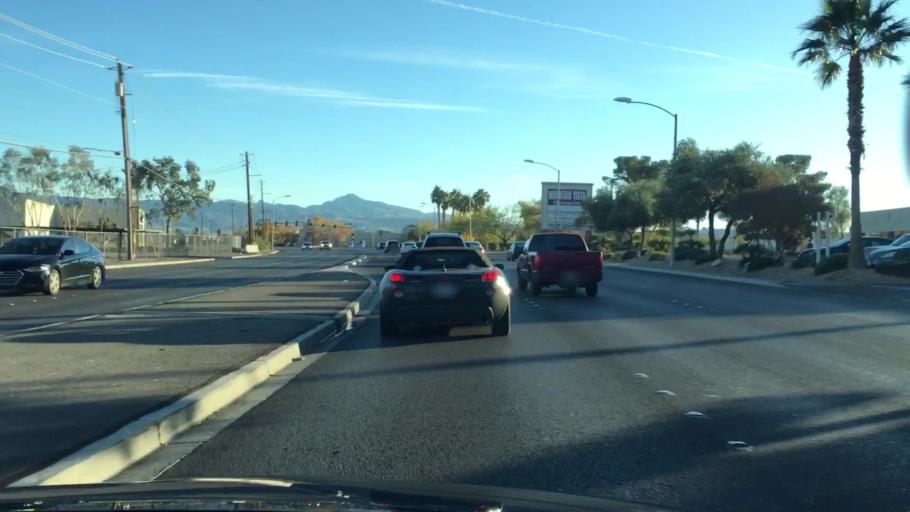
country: US
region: Nevada
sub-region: Clark County
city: Whitney
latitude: 36.0755
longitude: -115.0733
